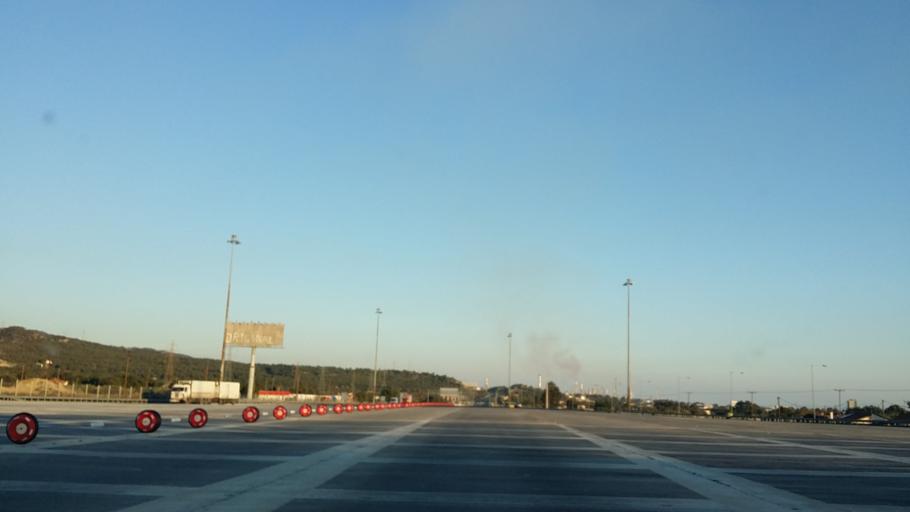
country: GR
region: Peloponnese
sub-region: Nomos Korinthias
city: Isthmia
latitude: 37.9250
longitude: 23.0329
